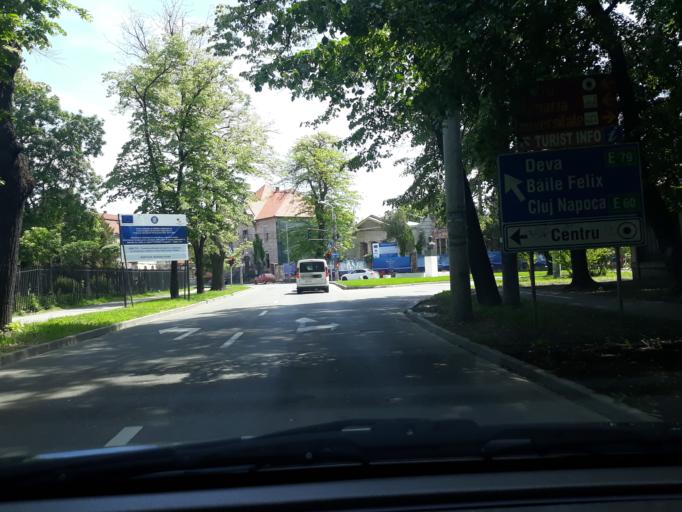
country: RO
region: Bihor
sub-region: Comuna Biharea
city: Oradea
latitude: 47.0502
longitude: 21.9244
